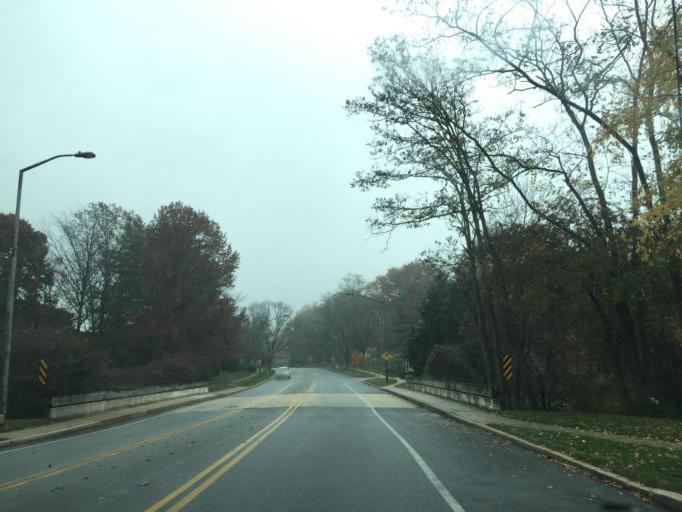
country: US
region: Maryland
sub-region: Howard County
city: Riverside
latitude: 39.1856
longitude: -76.8443
